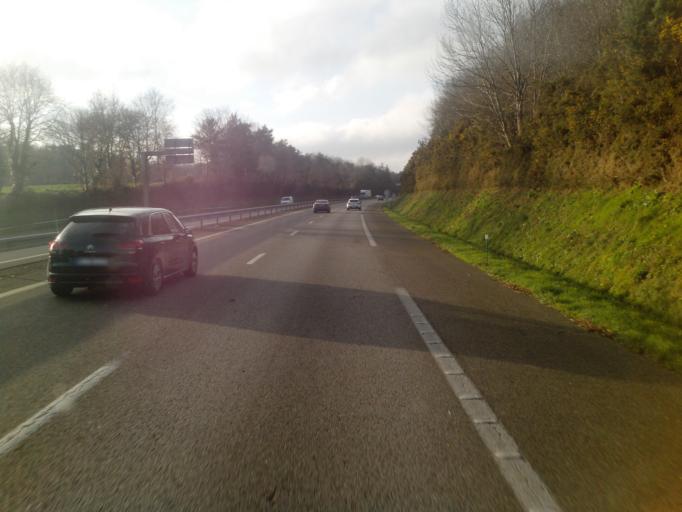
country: FR
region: Brittany
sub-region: Departement du Morbihan
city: Guillac
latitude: 47.9366
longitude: -2.4839
